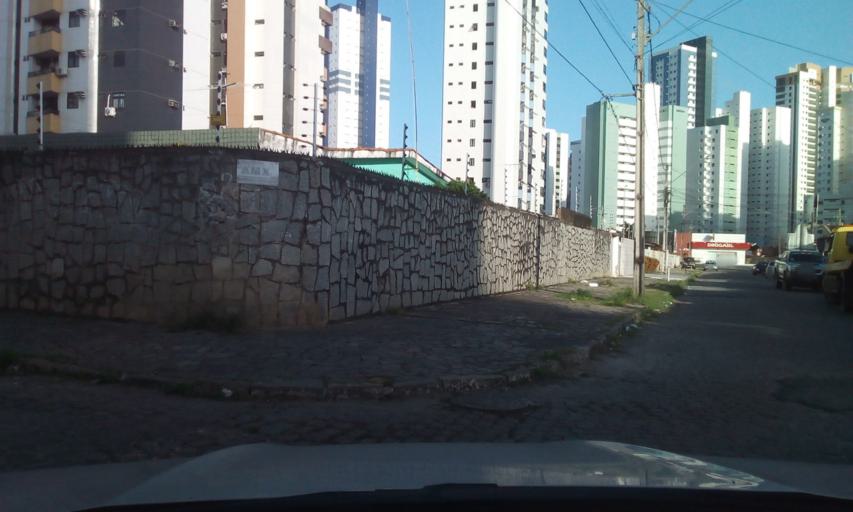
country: BR
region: Paraiba
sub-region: Joao Pessoa
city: Joao Pessoa
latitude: -7.1121
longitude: -34.8309
